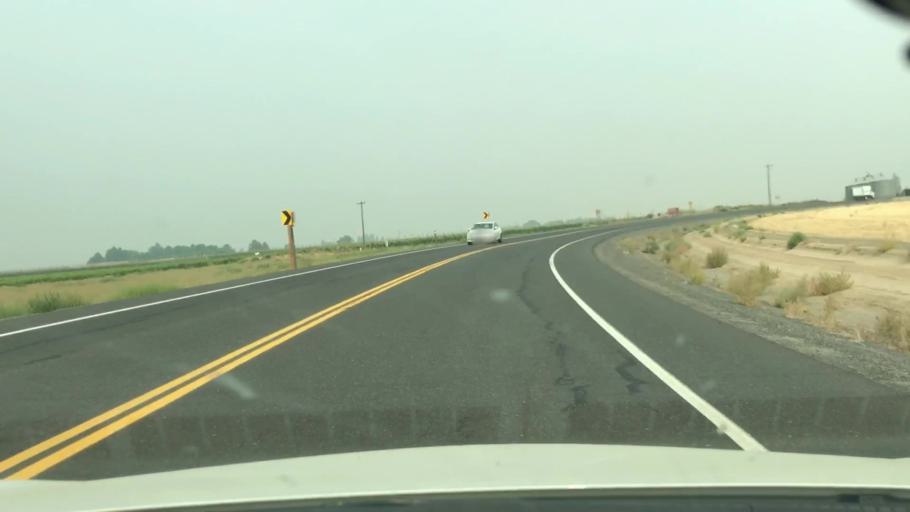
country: US
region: Washington
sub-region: Grant County
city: Quincy
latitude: 47.1646
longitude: -119.9381
